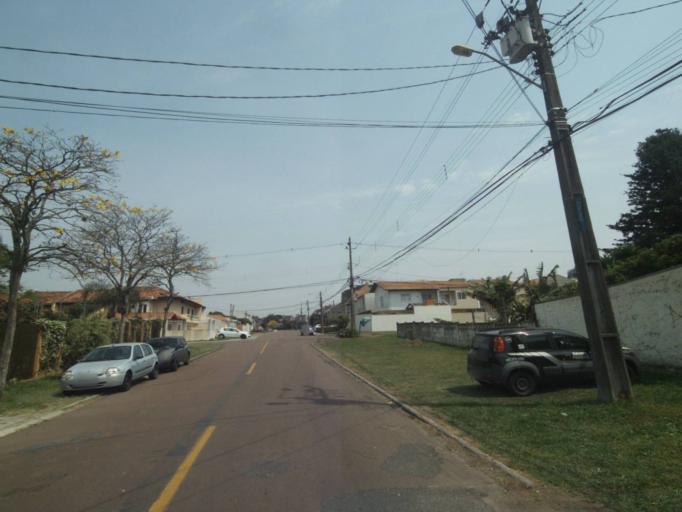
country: BR
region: Parana
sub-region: Sao Jose Dos Pinhais
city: Sao Jose dos Pinhais
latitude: -25.4924
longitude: -49.2094
